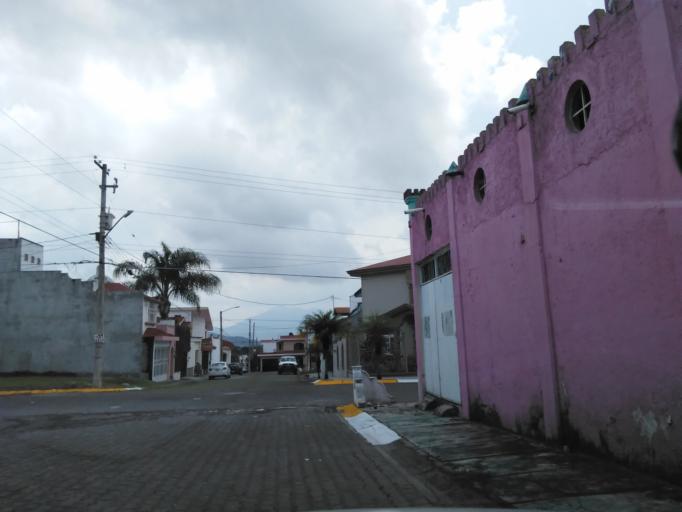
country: MX
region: Nayarit
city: Tepic
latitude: 21.5188
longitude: -104.9208
